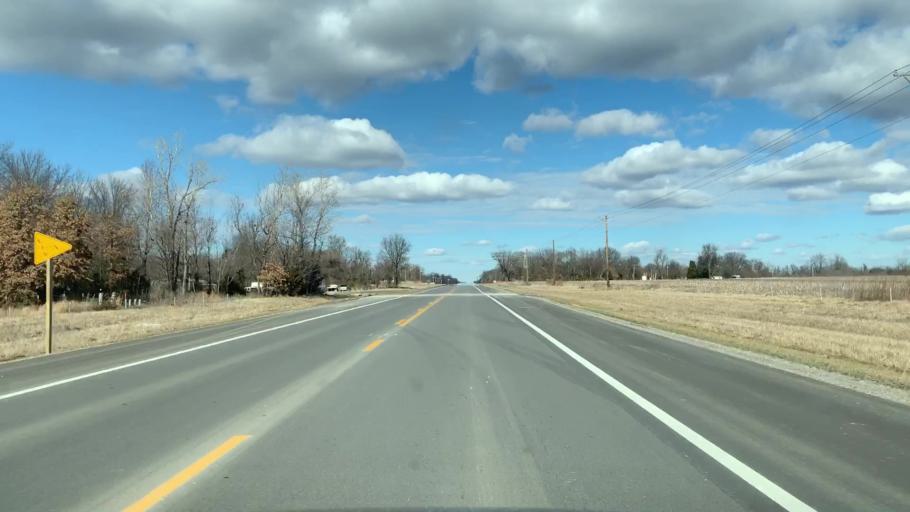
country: US
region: Kansas
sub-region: Cherokee County
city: Columbus
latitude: 37.2184
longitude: -94.8318
